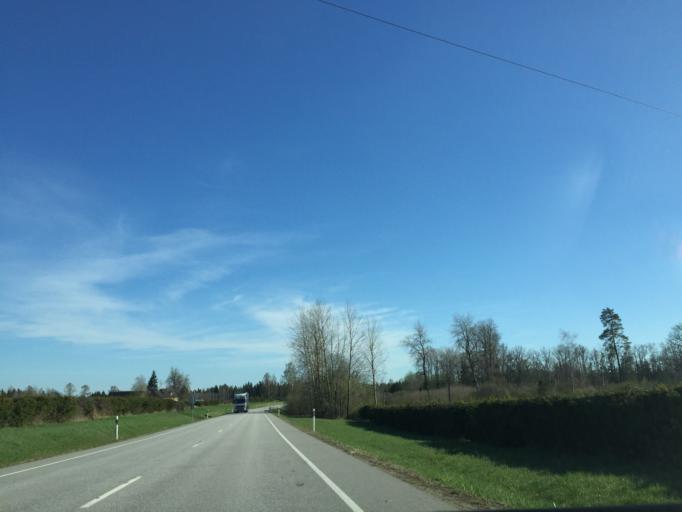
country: EE
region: Vorumaa
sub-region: Antsla vald
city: Vana-Antsla
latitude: 57.8998
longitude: 26.2882
